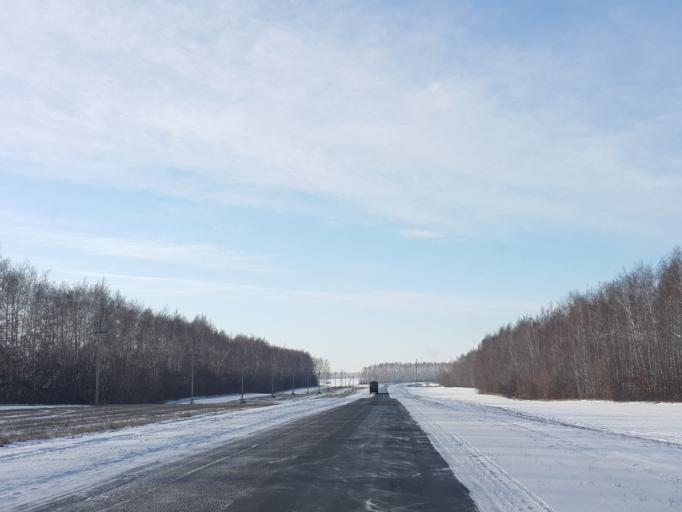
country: RU
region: Tambov
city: Znamenka
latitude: 52.3761
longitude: 41.3080
